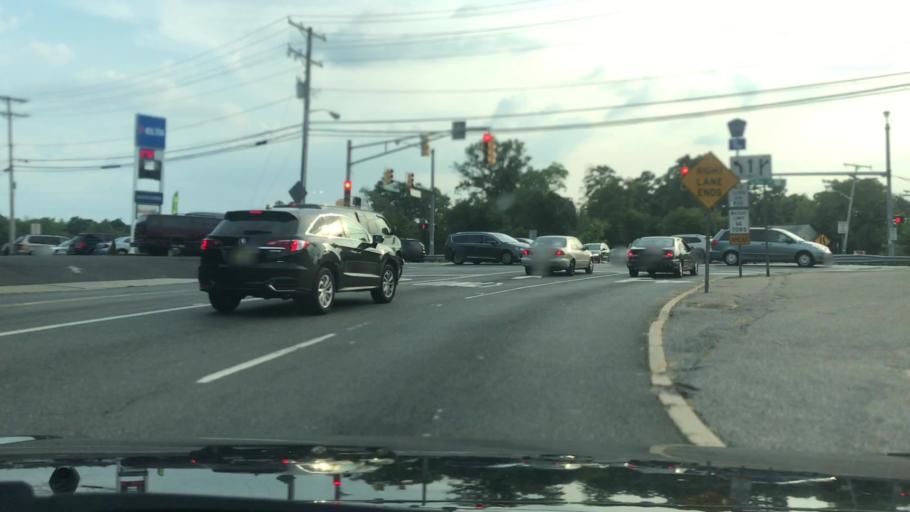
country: US
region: New Jersey
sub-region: Ocean County
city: Lakewood
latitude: 40.0866
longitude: -74.2148
